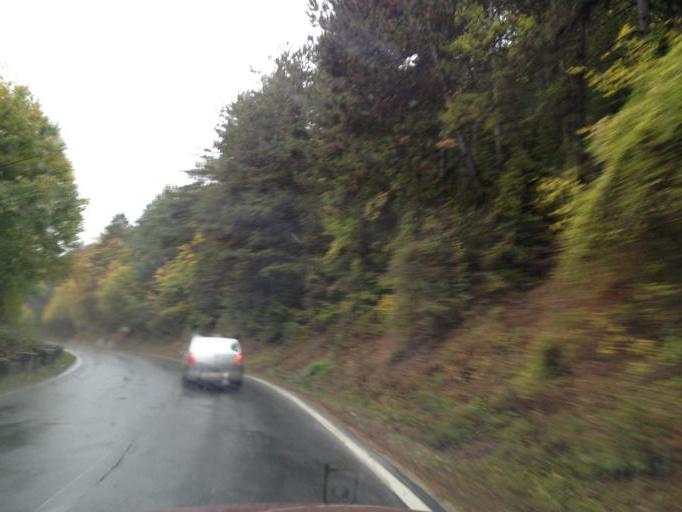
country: RO
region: Arges
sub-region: Comuna Dragoslavele
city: Dragoslavele
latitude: 45.3045
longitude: 25.1556
